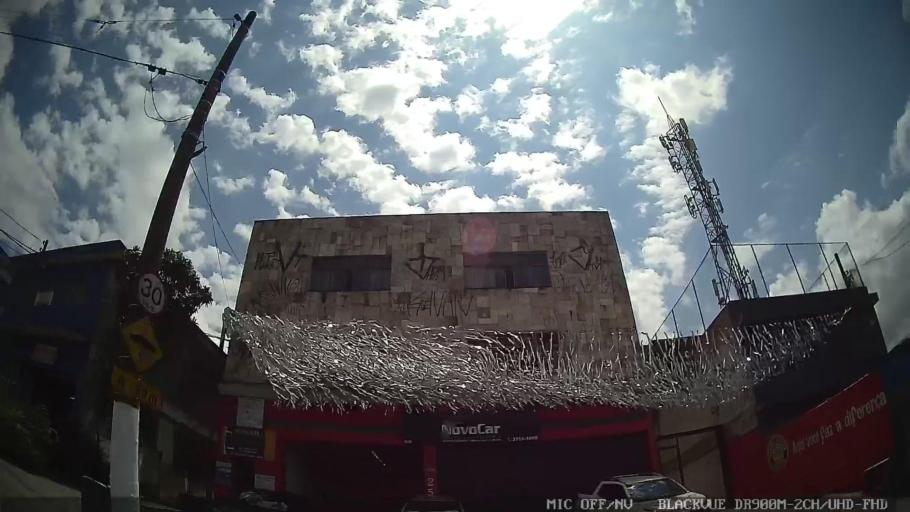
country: BR
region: Sao Paulo
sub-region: Ferraz De Vasconcelos
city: Ferraz de Vasconcelos
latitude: -23.5162
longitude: -46.4437
